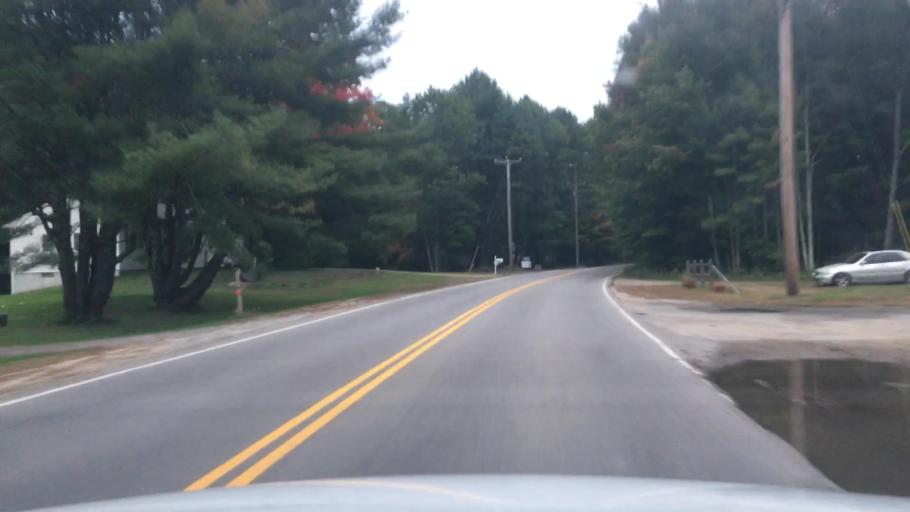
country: US
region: Maine
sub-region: York County
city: Buxton
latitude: 43.6339
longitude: -70.5082
